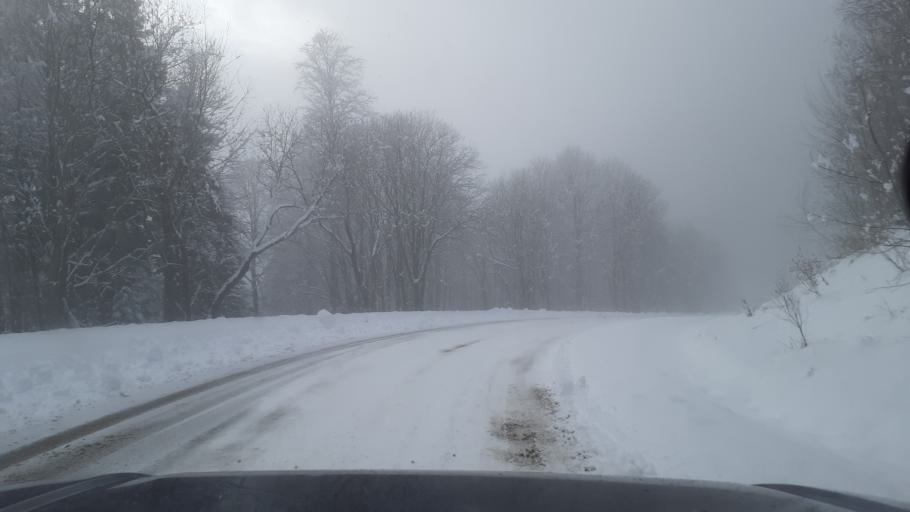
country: RU
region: Adygeya
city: Kamennomostskiy
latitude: 44.0108
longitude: 40.0278
